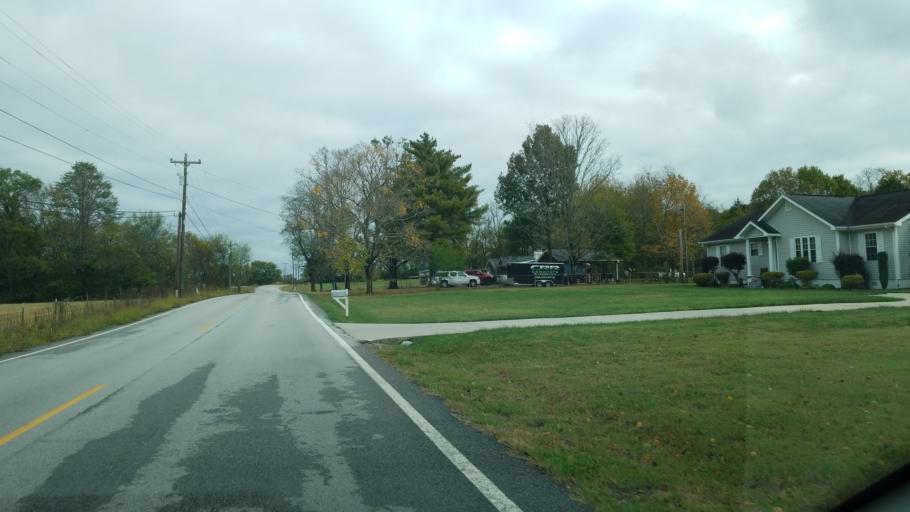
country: US
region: Tennessee
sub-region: Hamilton County
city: Lakesite
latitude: 35.1872
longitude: -85.0219
